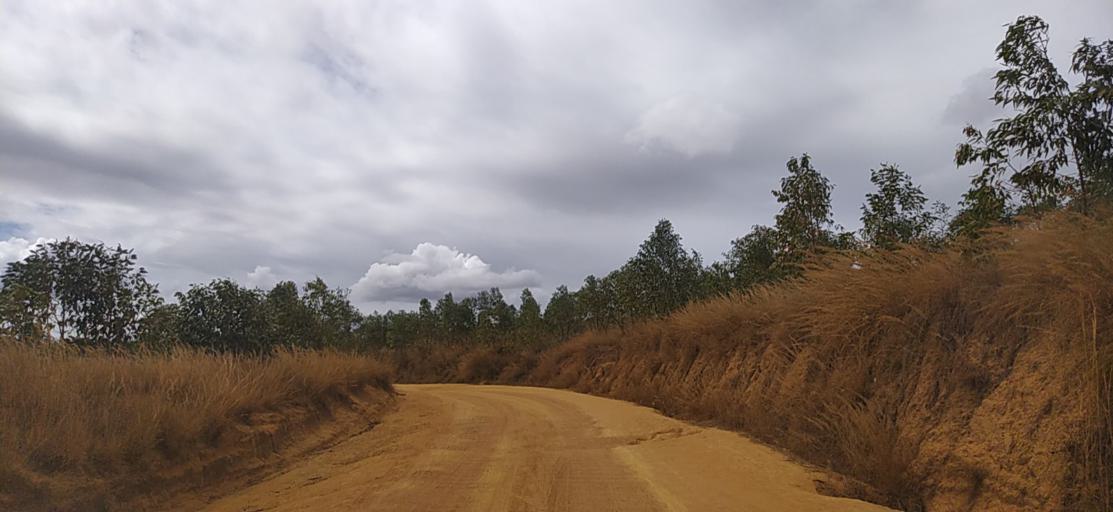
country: MG
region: Alaotra Mangoro
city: Ambatondrazaka
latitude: -17.9509
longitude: 48.2491
